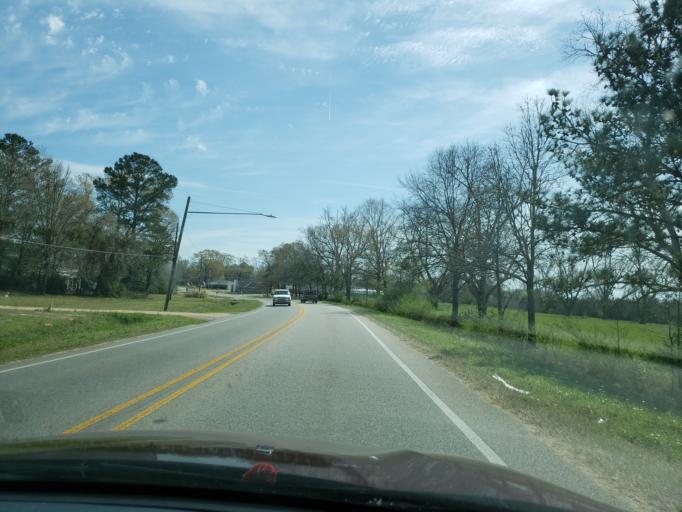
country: US
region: Alabama
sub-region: Elmore County
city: Tallassee
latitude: 32.5689
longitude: -85.9377
